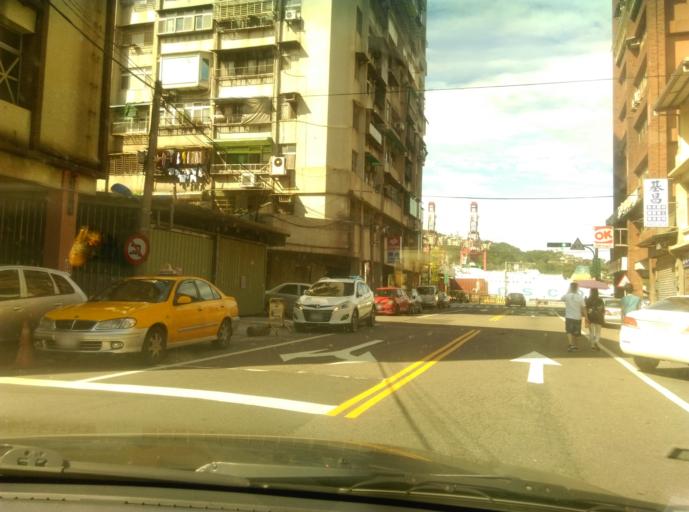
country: TW
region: Taiwan
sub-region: Keelung
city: Keelung
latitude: 25.1379
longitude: 121.7513
